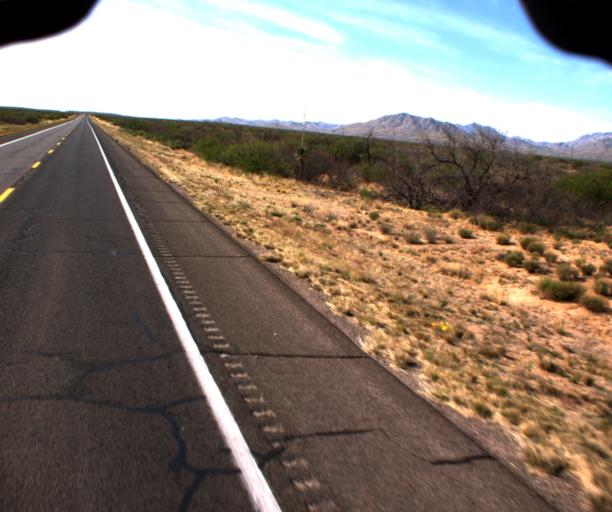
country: US
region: Arizona
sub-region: Graham County
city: Swift Trail Junction
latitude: 32.6608
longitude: -109.7008
